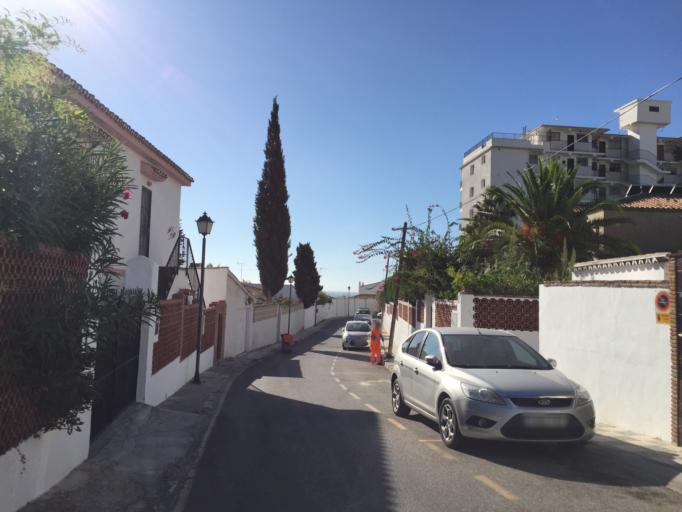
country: ES
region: Andalusia
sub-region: Provincia de Malaga
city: Nerja
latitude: 36.7533
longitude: -3.8720
